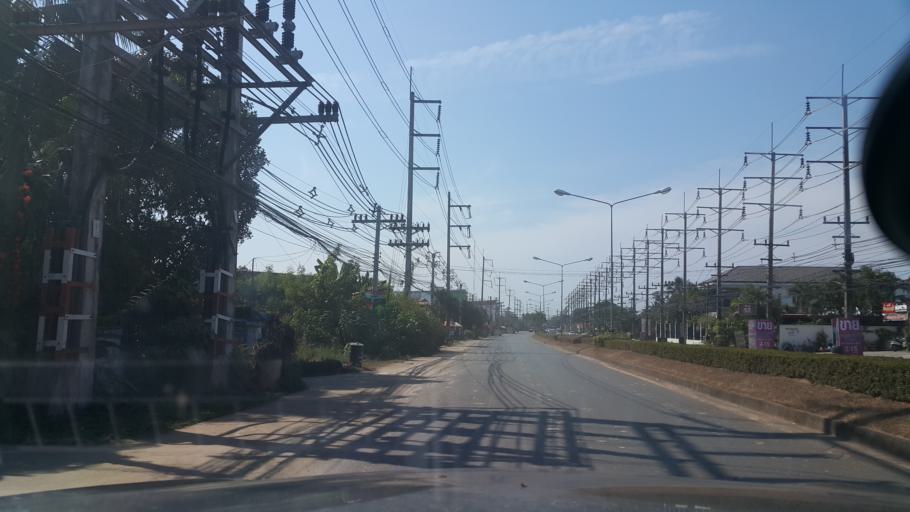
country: TH
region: Changwat Udon Thani
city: Udon Thani
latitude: 17.4491
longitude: 102.7888
